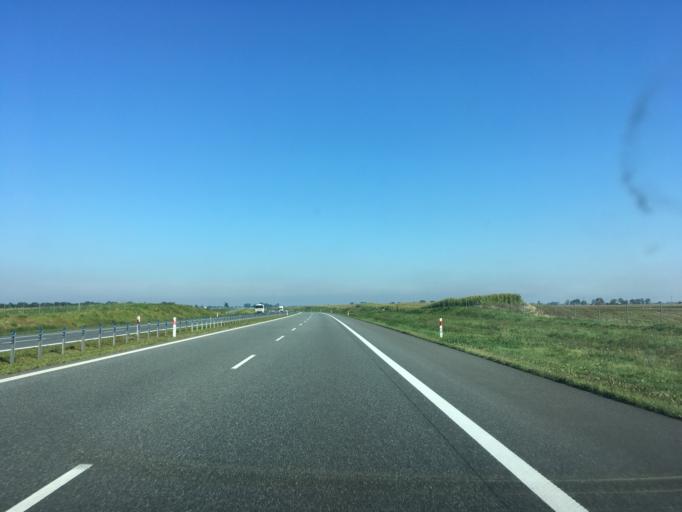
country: PL
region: Kujawsko-Pomorskie
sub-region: Powiat wabrzeski
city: Pluznica
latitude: 53.1955
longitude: 18.7396
